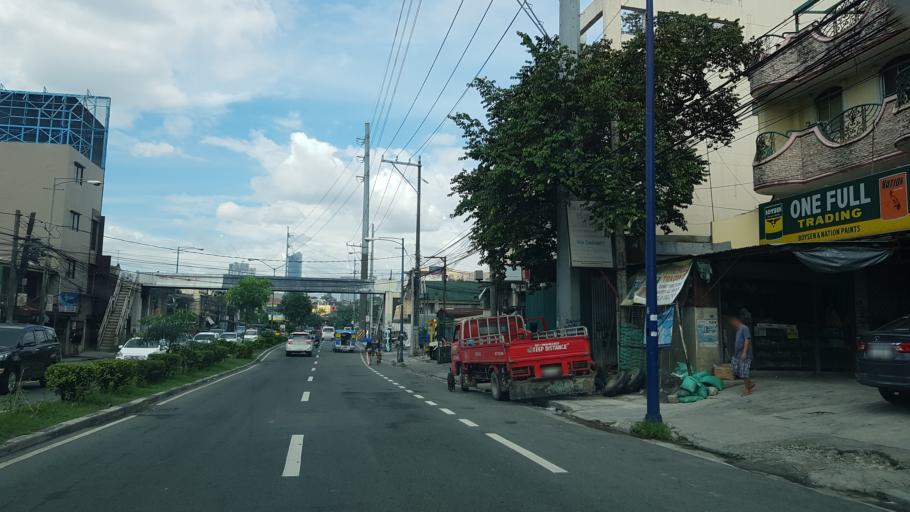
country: PH
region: Metro Manila
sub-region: Makati City
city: Makati City
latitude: 14.5602
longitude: 121.0480
